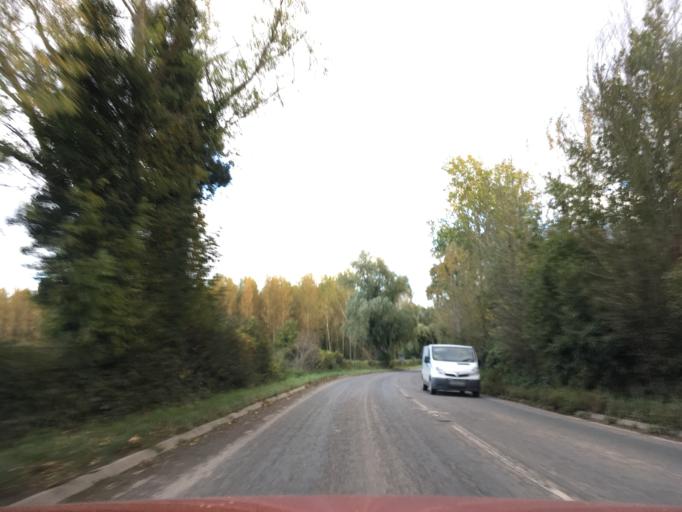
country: GB
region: England
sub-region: Herefordshire
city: Withington
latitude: 52.0624
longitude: -2.6267
